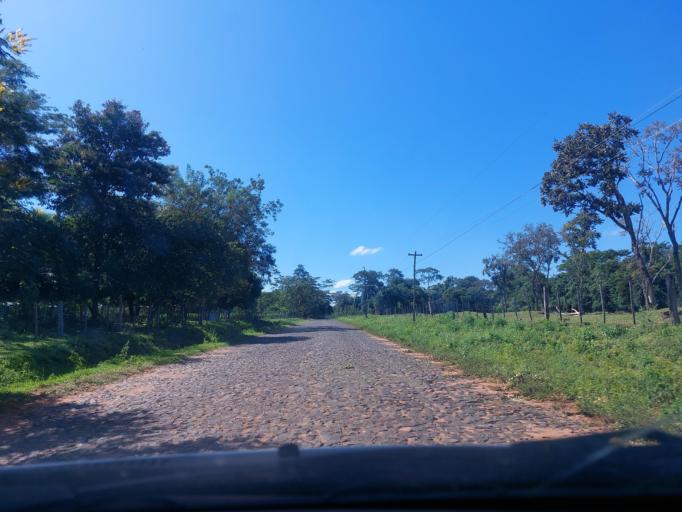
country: PY
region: San Pedro
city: Itacurubi del Rosario
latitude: -24.5751
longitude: -56.5988
